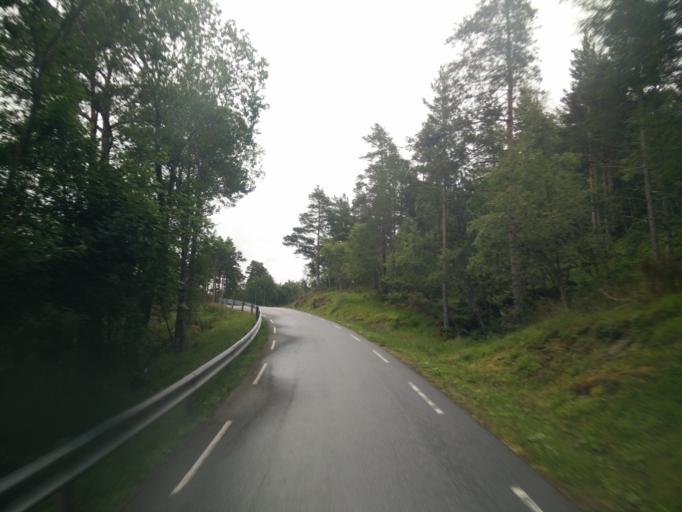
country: NO
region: More og Romsdal
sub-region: Kristiansund
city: Rensvik
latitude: 63.0370
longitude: 7.9163
